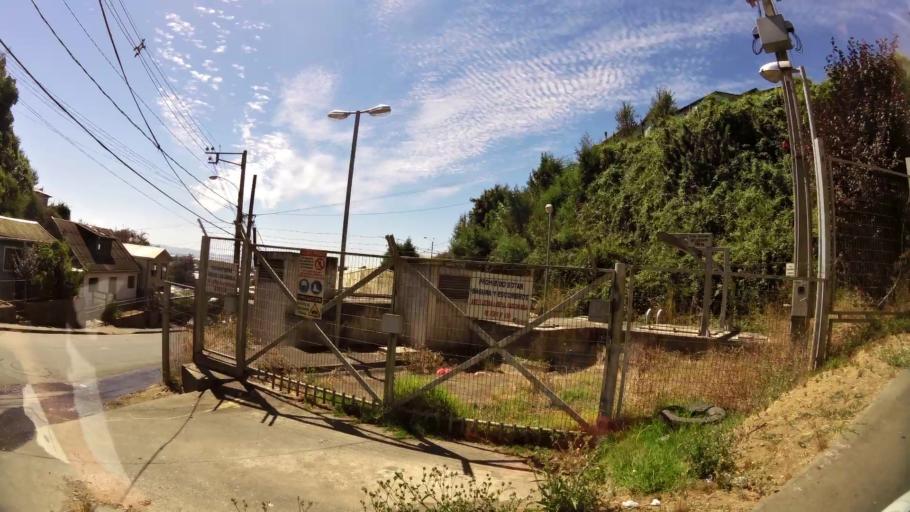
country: CL
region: Biobio
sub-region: Provincia de Concepcion
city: Penco
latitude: -36.7391
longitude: -72.9881
